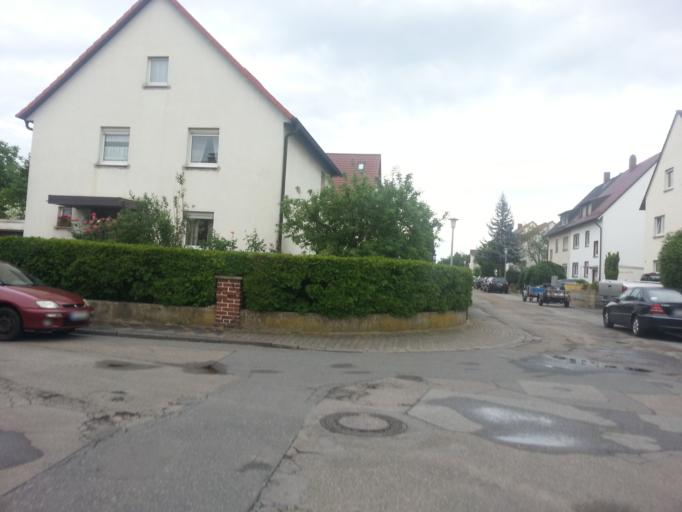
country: DE
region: Rheinland-Pfalz
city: Altrip
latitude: 49.4659
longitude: 8.5021
